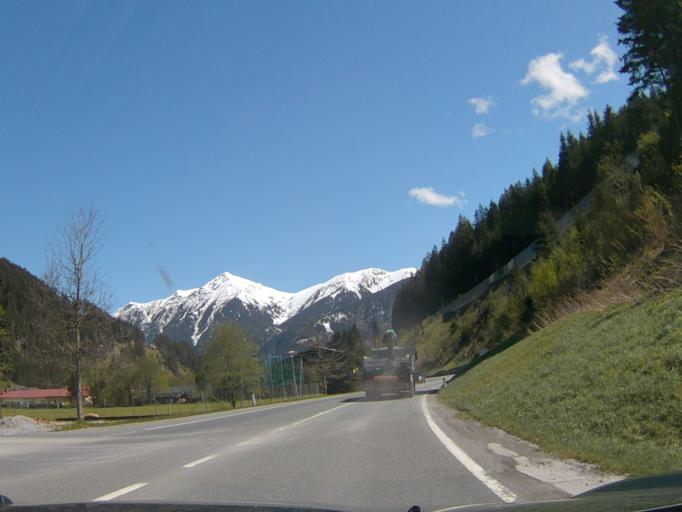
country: AT
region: Salzburg
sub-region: Politischer Bezirk Sankt Johann im Pongau
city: Bad Gastein
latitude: 47.0964
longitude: 13.1245
